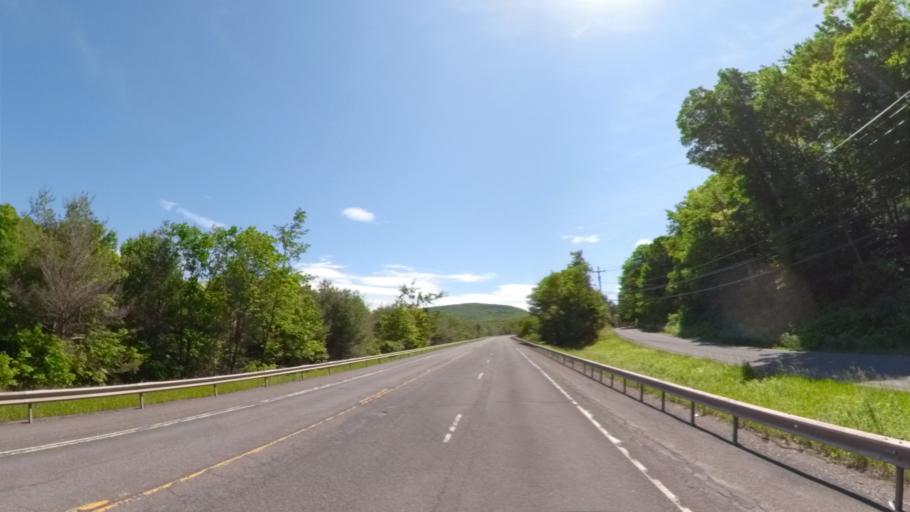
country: US
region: New York
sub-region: Delaware County
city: Stamford
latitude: 42.1512
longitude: -74.5119
